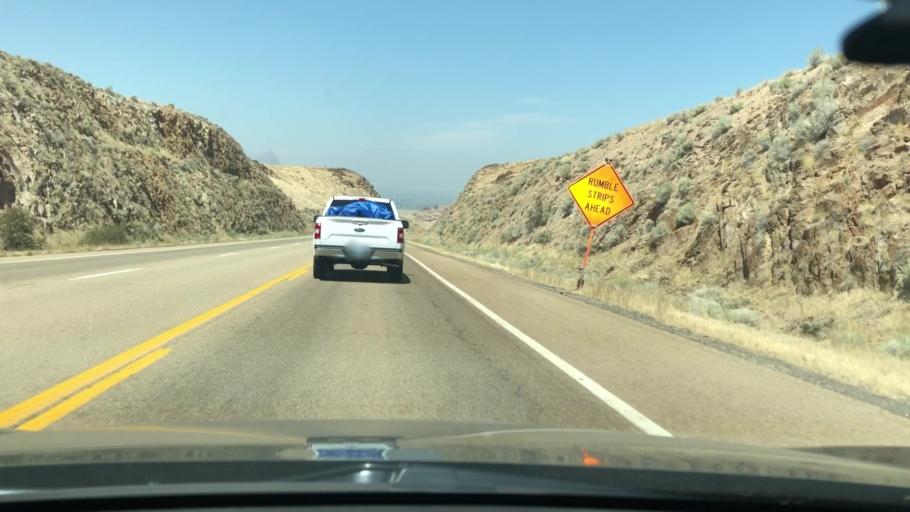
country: US
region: Idaho
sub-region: Owyhee County
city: Marsing
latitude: 43.4294
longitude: -116.8595
